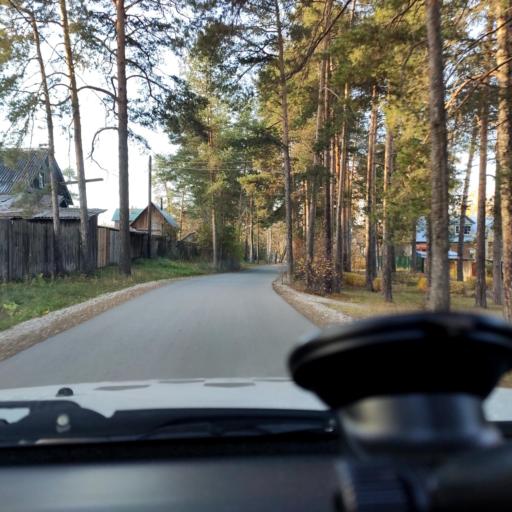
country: RU
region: Perm
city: Perm
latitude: 58.0562
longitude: 56.2998
